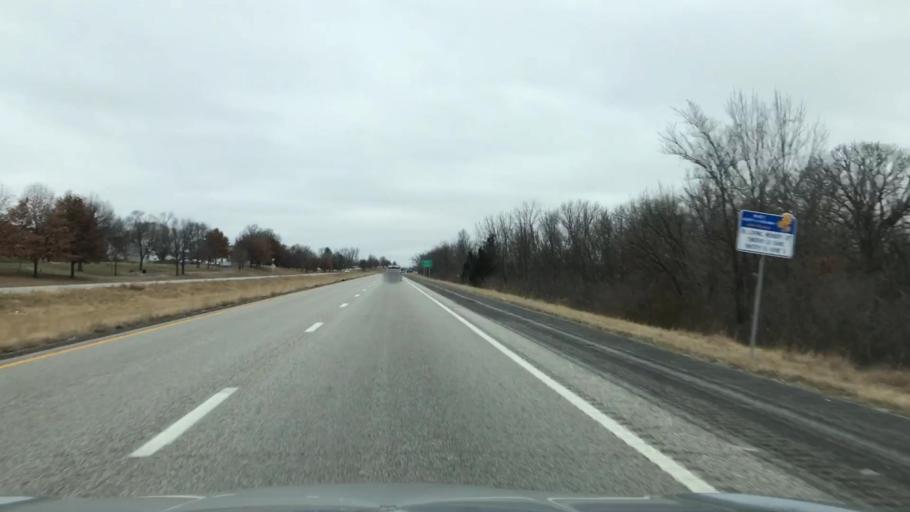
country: US
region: Missouri
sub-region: Clay County
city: Liberty
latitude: 39.2212
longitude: -94.4101
